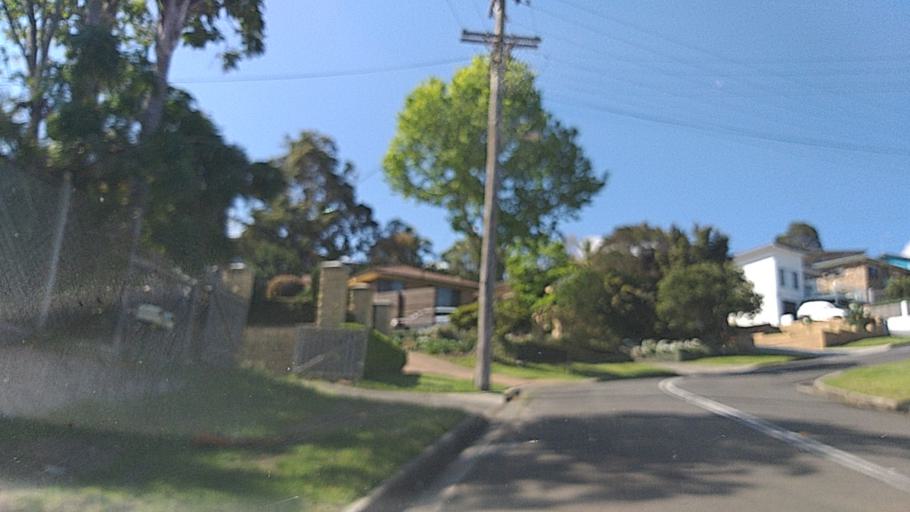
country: AU
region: New South Wales
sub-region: Wollongong
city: Cordeaux Heights
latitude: -34.4538
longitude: 150.8346
